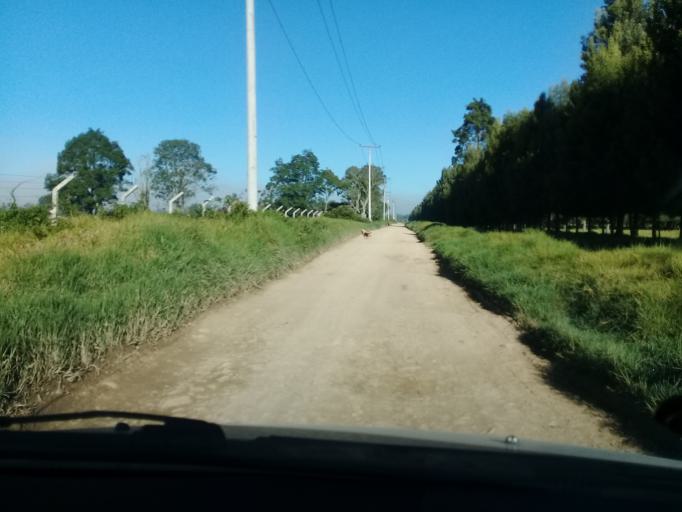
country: CO
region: Cundinamarca
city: Funza
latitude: 4.7582
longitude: -74.2262
